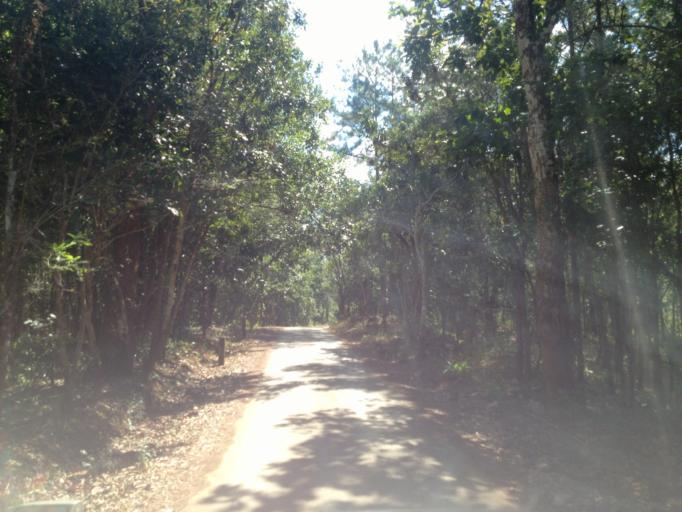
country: TH
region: Mae Hong Son
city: Ban Huai I Huak
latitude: 18.1085
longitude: 98.1710
